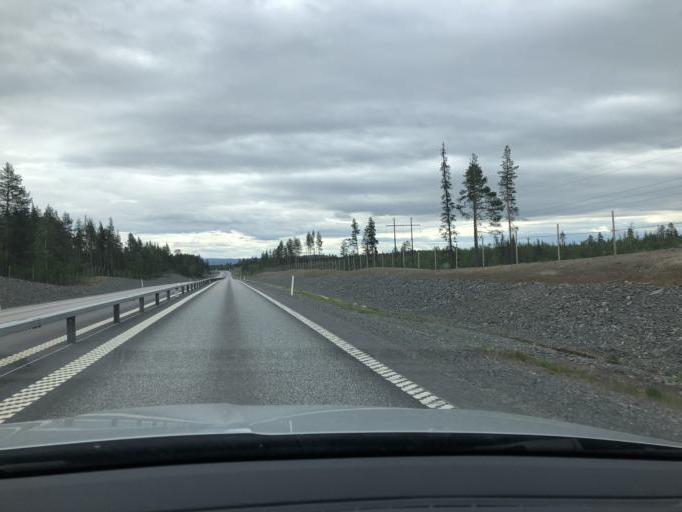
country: SE
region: Norrbotten
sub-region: Gallivare Kommun
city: Malmberget
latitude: 67.6818
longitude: 20.8721
